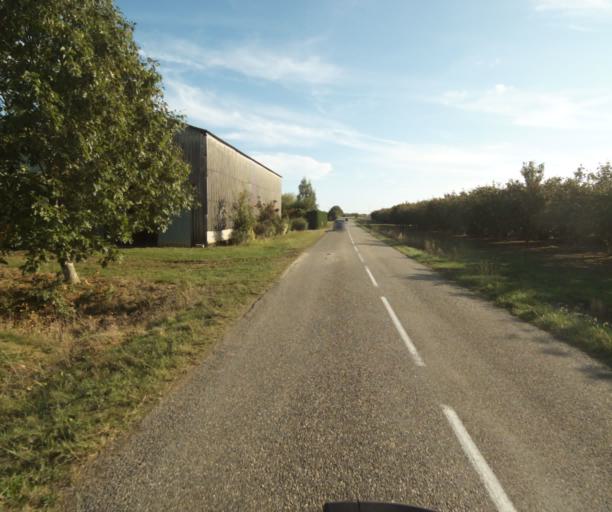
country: FR
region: Midi-Pyrenees
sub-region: Departement du Tarn-et-Garonne
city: Finhan
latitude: 43.9012
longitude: 1.1246
